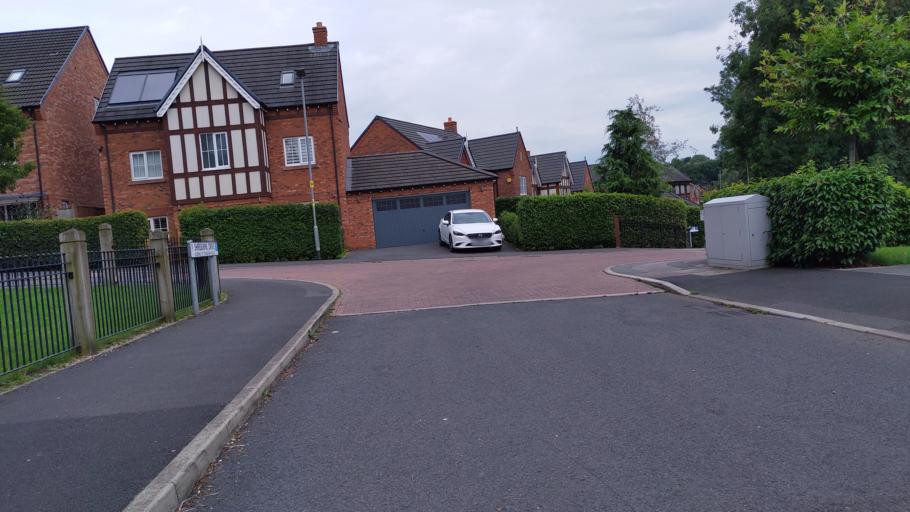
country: GB
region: England
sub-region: Lancashire
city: Chorley
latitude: 53.6384
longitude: -2.6243
